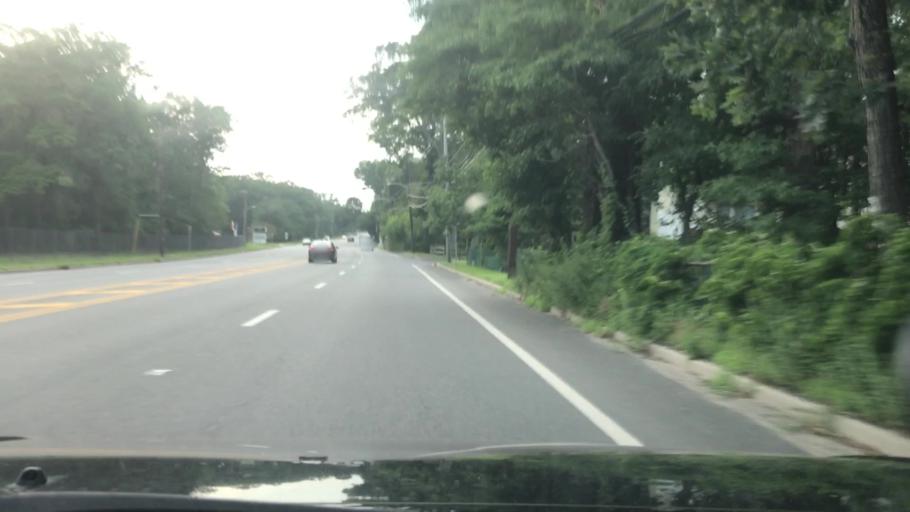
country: US
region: New Jersey
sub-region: Ocean County
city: Lakewood
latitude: 40.1130
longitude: -74.2441
